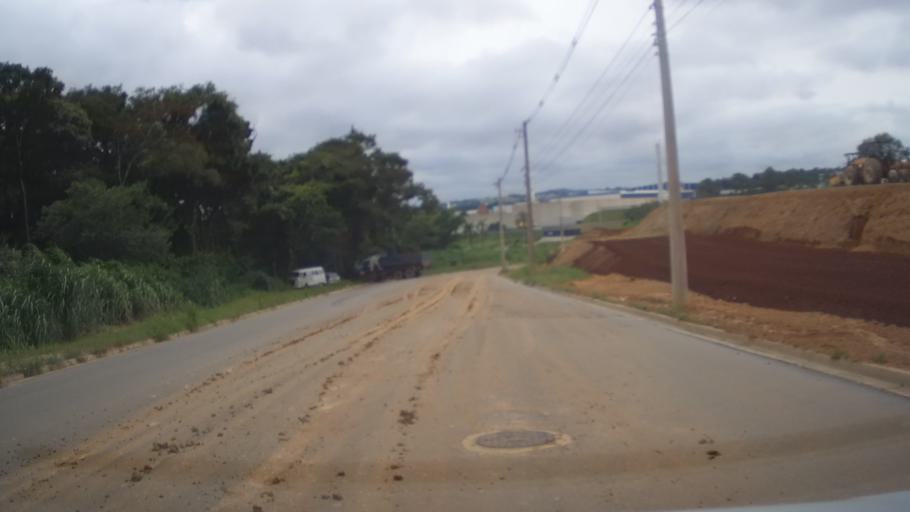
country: BR
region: Sao Paulo
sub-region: Vinhedo
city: Vinhedo
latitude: -23.0739
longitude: -47.0060
